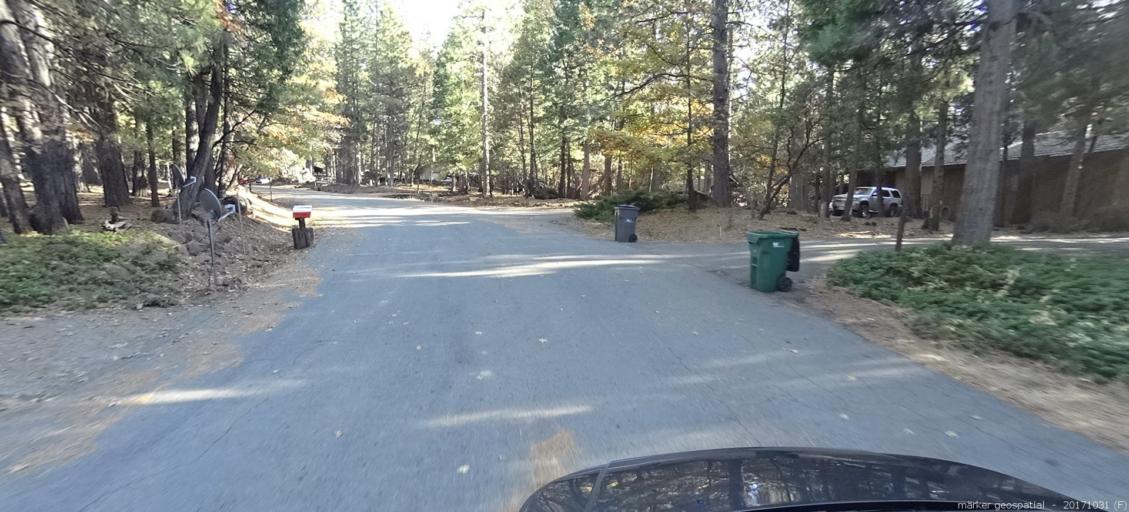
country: US
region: California
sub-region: Shasta County
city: Shingletown
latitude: 40.5021
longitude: -121.9145
